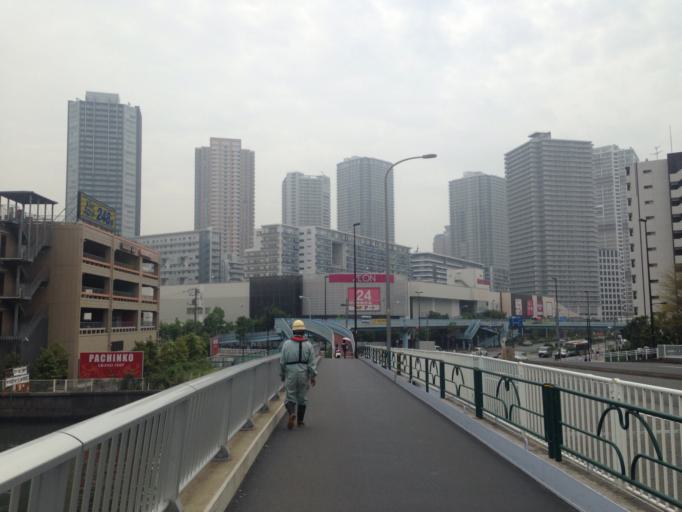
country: JP
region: Tokyo
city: Urayasu
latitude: 35.6504
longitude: 139.8009
